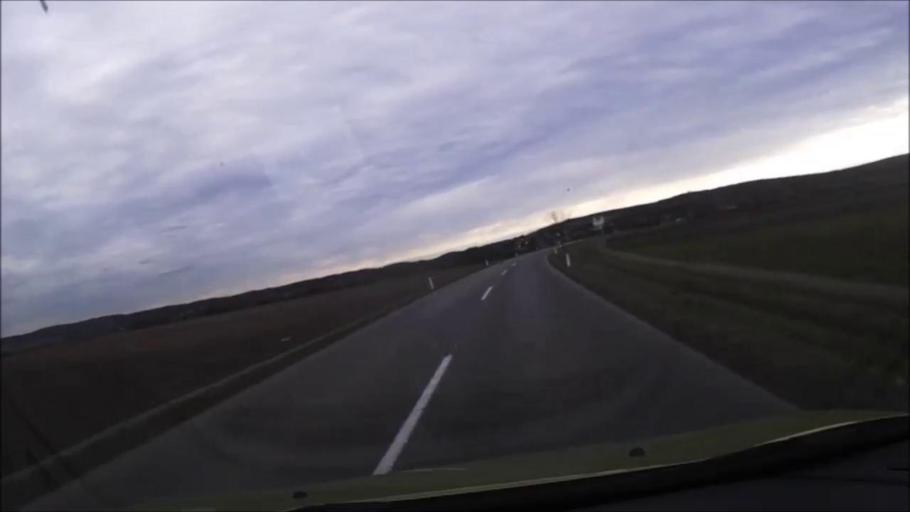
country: AT
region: Burgenland
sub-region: Eisenstadt-Umgebung
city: Loretto
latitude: 47.9220
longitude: 16.5049
